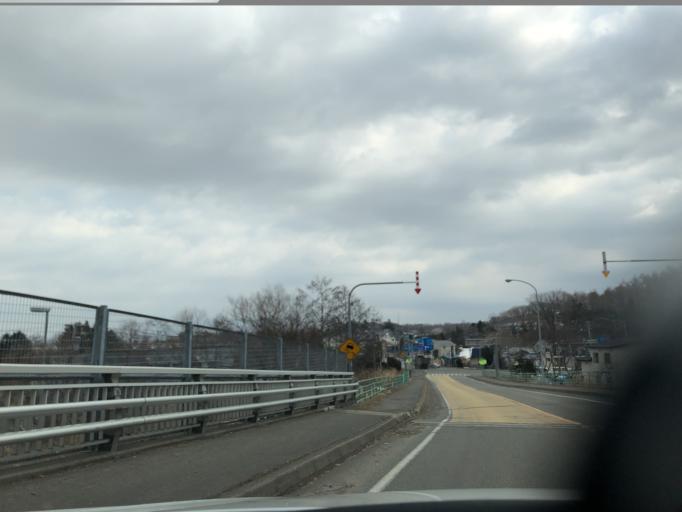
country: JP
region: Hokkaido
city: Chitose
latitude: 42.7620
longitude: 141.8104
